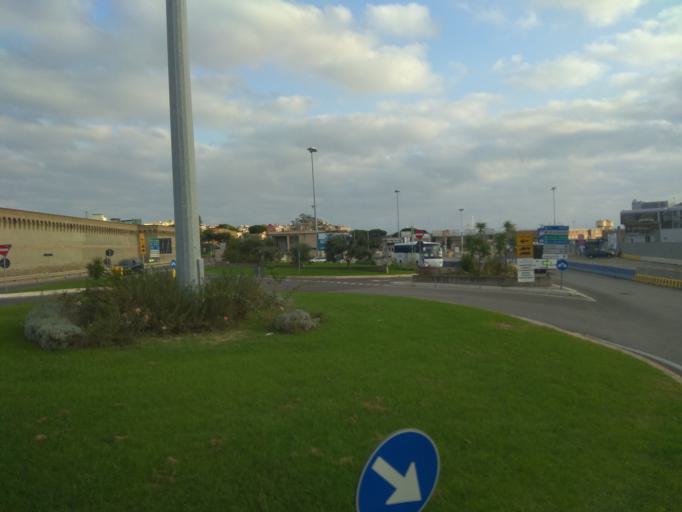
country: IT
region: Latium
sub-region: Citta metropolitana di Roma Capitale
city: Civitavecchia
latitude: 42.0984
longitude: 11.7855
